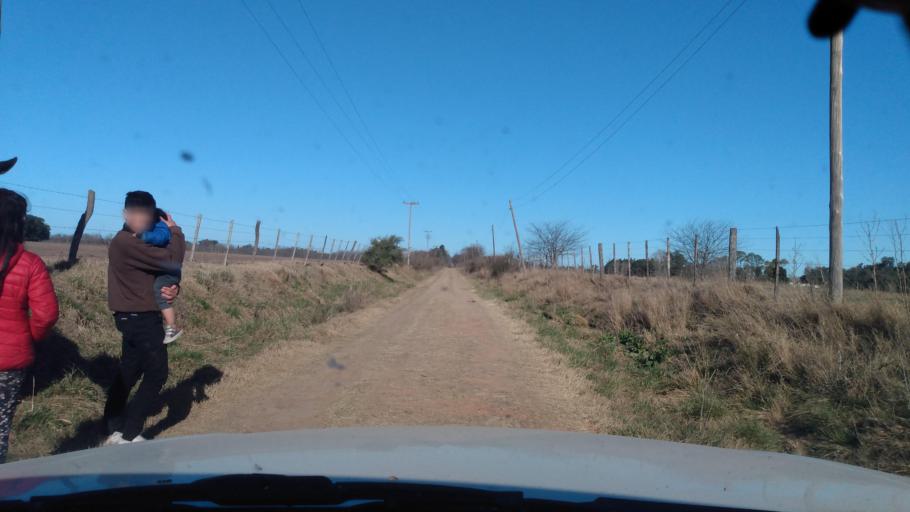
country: AR
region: Buenos Aires
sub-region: Partido de Mercedes
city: Mercedes
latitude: -34.6366
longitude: -59.3761
